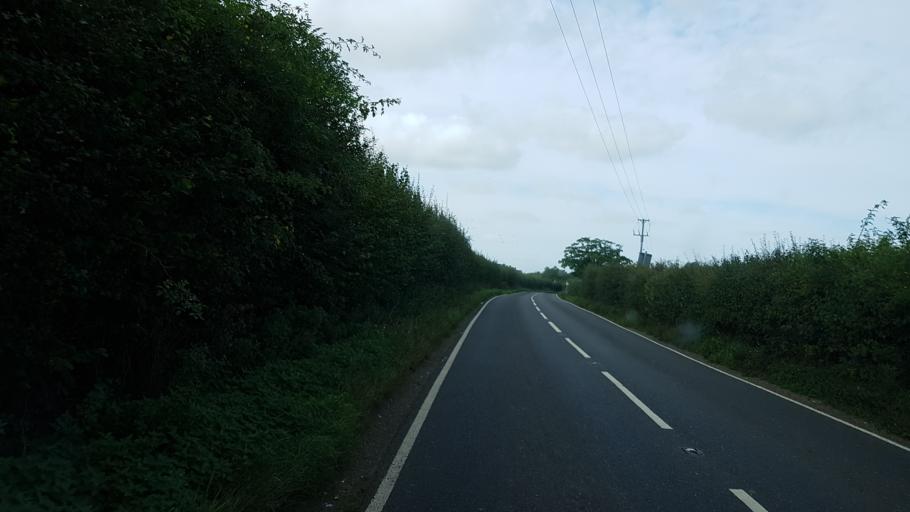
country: GB
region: England
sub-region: Kent
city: Maidstone
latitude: 51.2267
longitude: 0.5583
